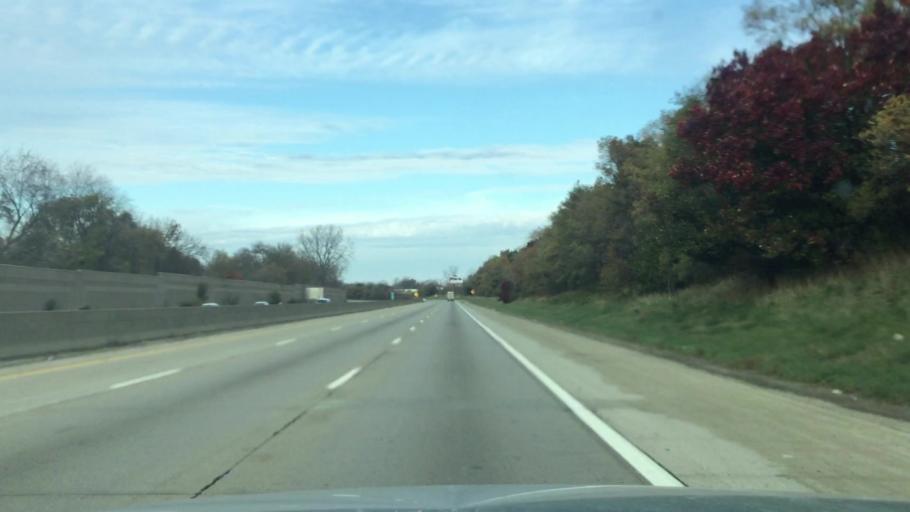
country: US
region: Michigan
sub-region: Washtenaw County
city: Ypsilanti
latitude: 42.2276
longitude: -83.5723
